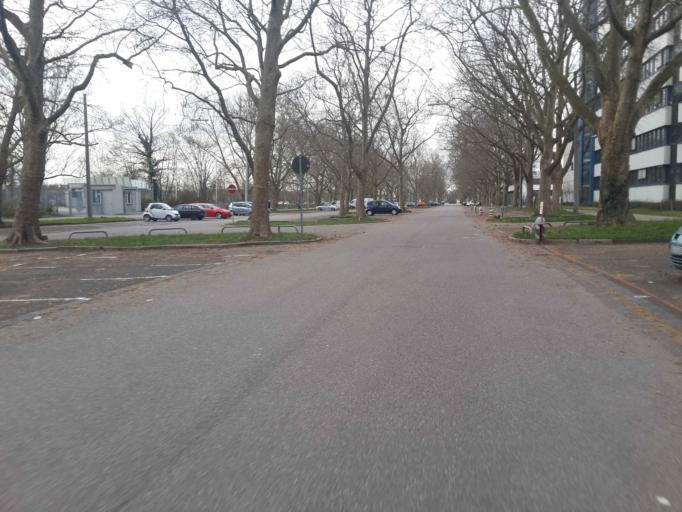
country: DE
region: Baden-Wuerttemberg
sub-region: Regierungsbezirk Stuttgart
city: Heilbronn
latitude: 49.1352
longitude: 9.2052
